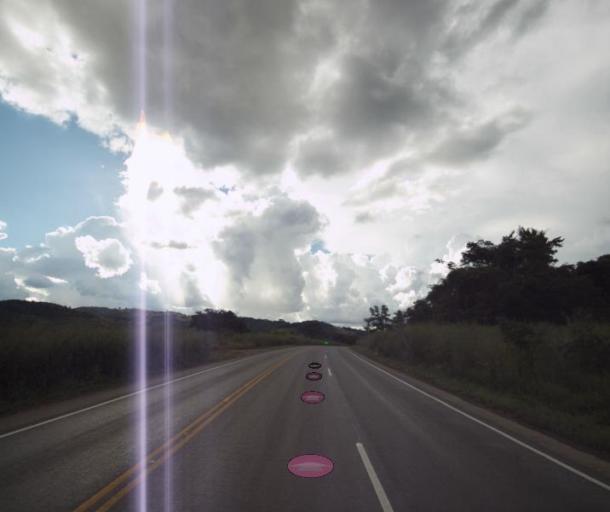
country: BR
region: Goias
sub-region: Rialma
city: Rialma
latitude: -15.2521
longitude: -49.5542
